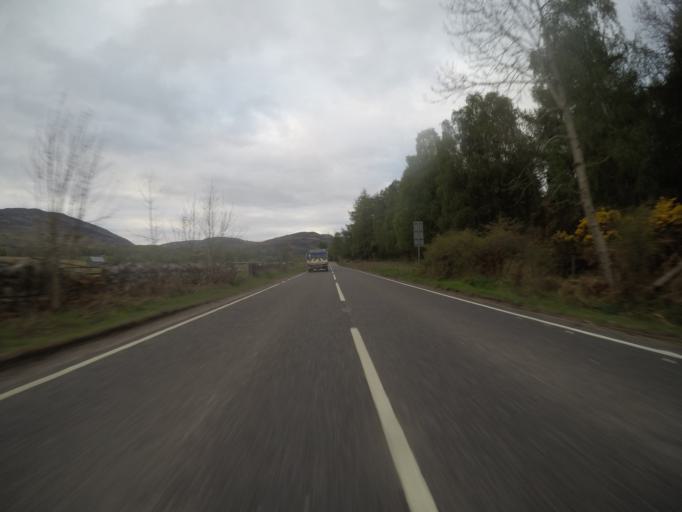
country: GB
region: Scotland
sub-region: Highland
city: Spean Bridge
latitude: 57.1339
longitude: -4.6894
